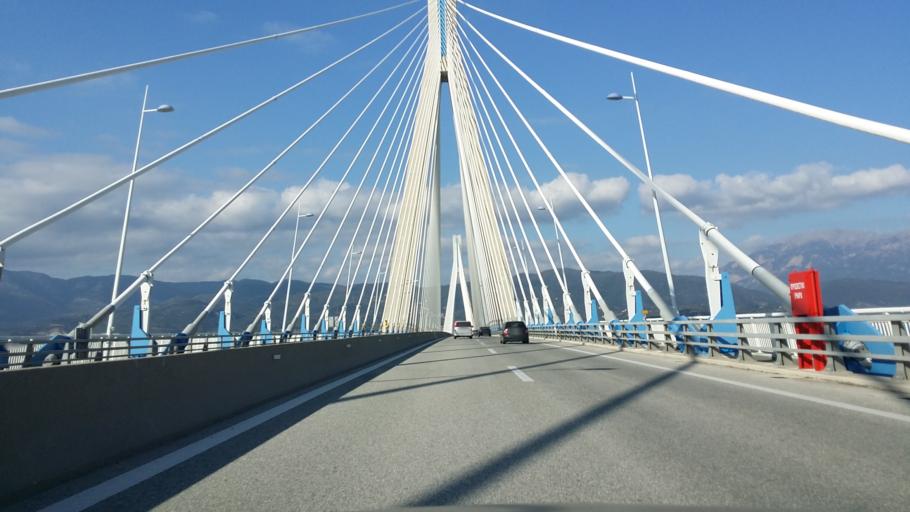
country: GR
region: West Greece
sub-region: Nomos Aitolias kai Akarnanias
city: Antirrio
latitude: 38.3205
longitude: 21.7731
